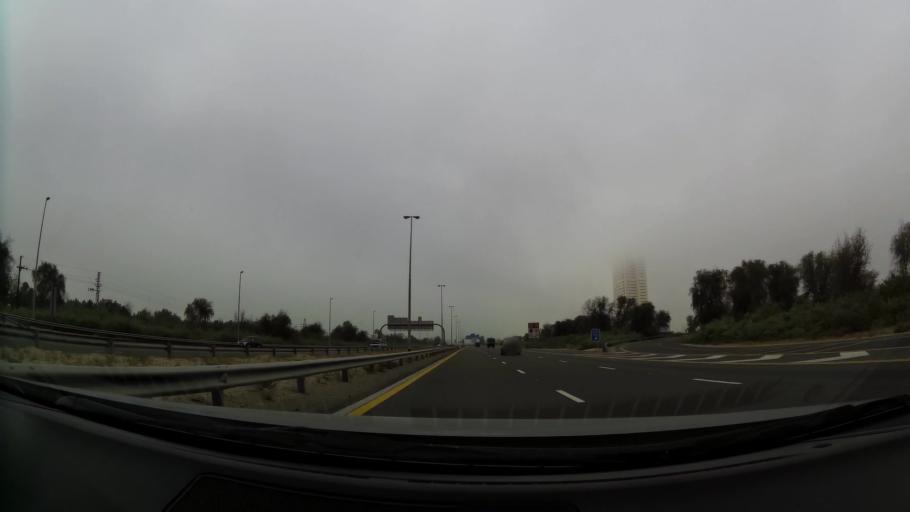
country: AE
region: Dubai
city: Dubai
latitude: 25.1006
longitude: 55.3815
